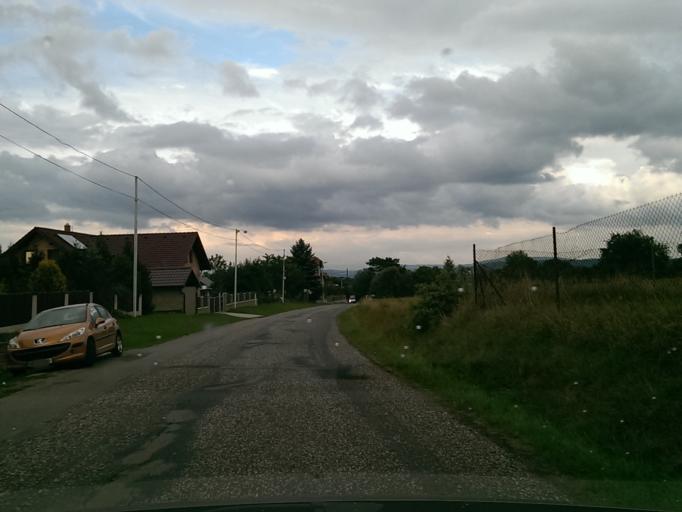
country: CZ
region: Central Bohemia
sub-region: Okres Mlada Boleslav
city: Zd'ar
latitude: 50.5384
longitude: 15.0335
